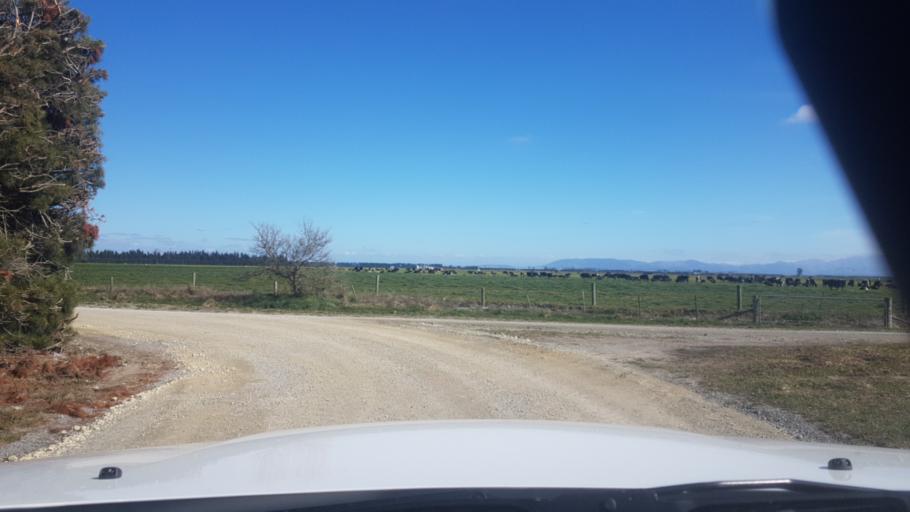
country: NZ
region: Canterbury
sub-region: Ashburton District
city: Tinwald
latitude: -44.1024
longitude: 171.4406
